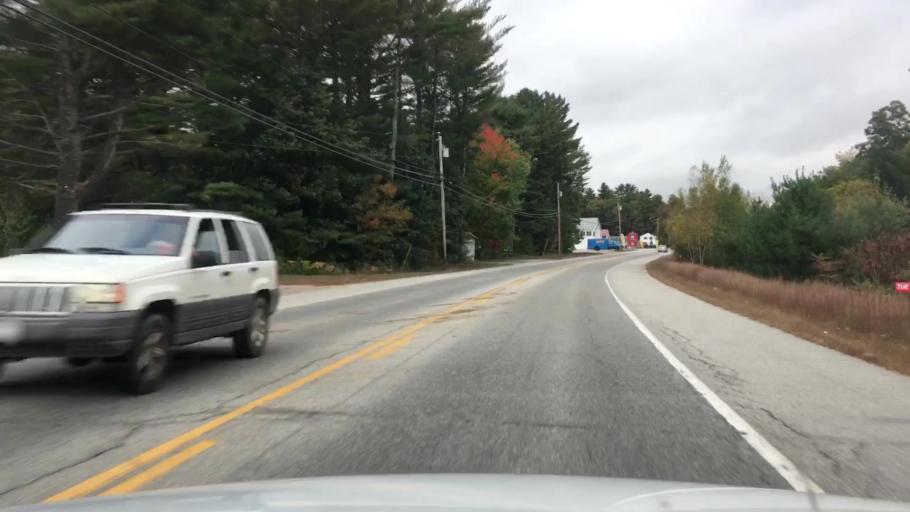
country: US
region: Maine
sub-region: Oxford County
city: Oxford
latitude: 44.1688
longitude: -70.5067
